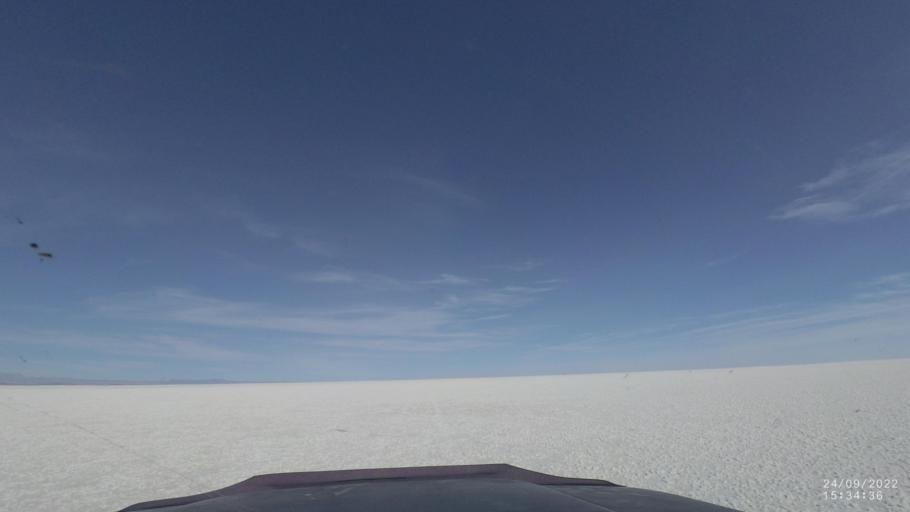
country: BO
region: Potosi
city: Colchani
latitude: -20.1262
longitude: -67.2611
